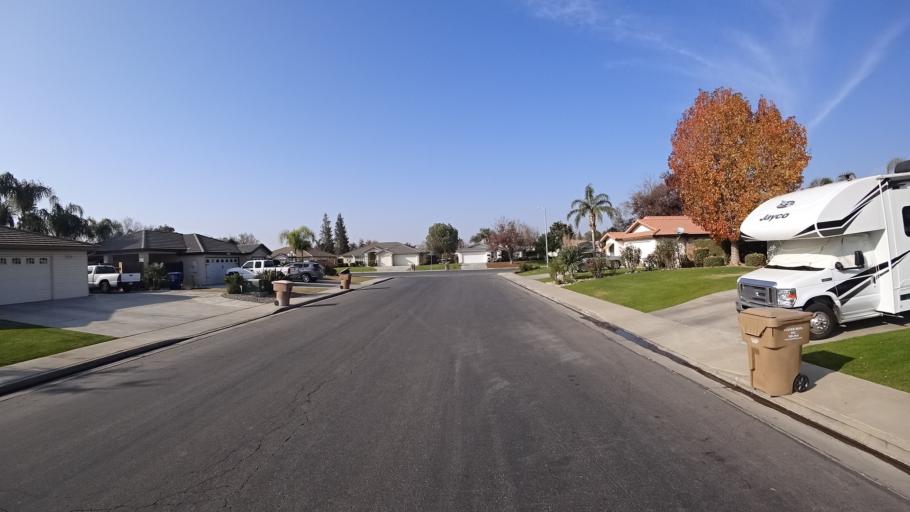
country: US
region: California
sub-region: Kern County
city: Greenacres
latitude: 35.4059
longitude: -119.1130
